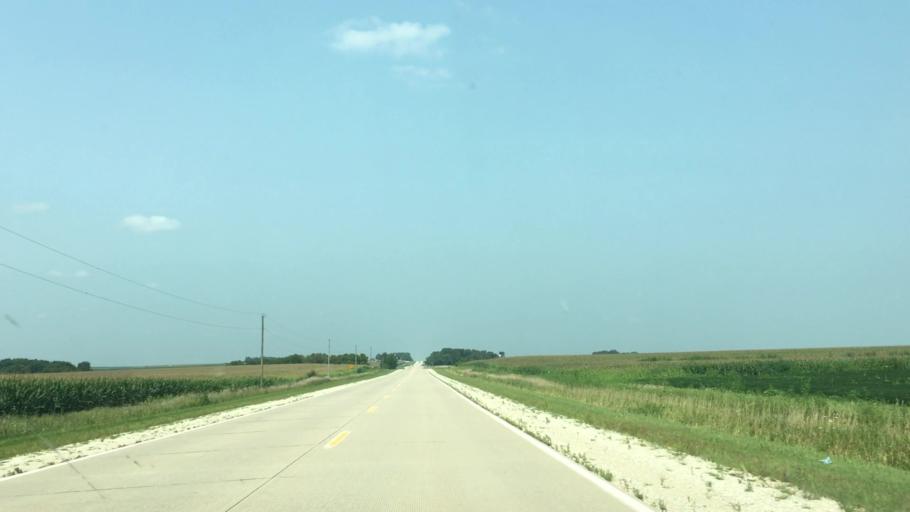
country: US
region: Iowa
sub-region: Fayette County
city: Fayette
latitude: 42.7514
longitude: -91.8042
